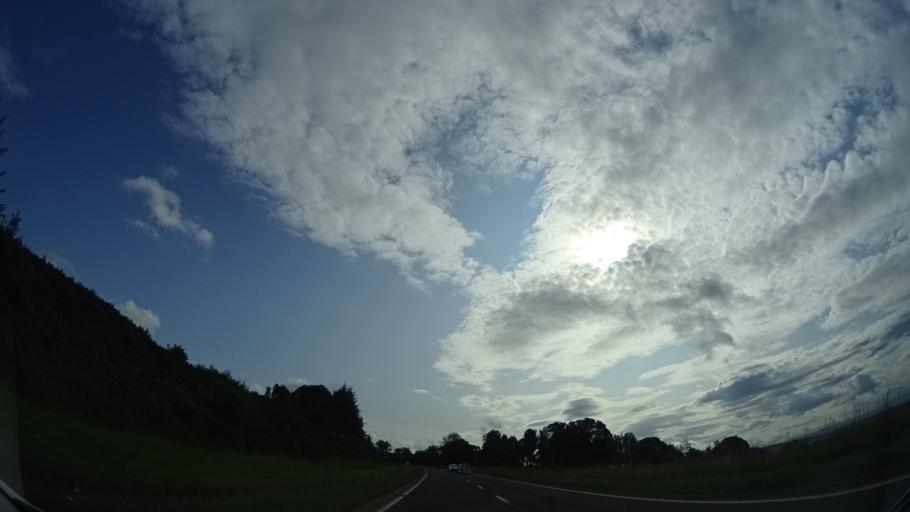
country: GB
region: Scotland
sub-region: Highland
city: Muir of Ord
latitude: 57.5583
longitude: -4.5055
